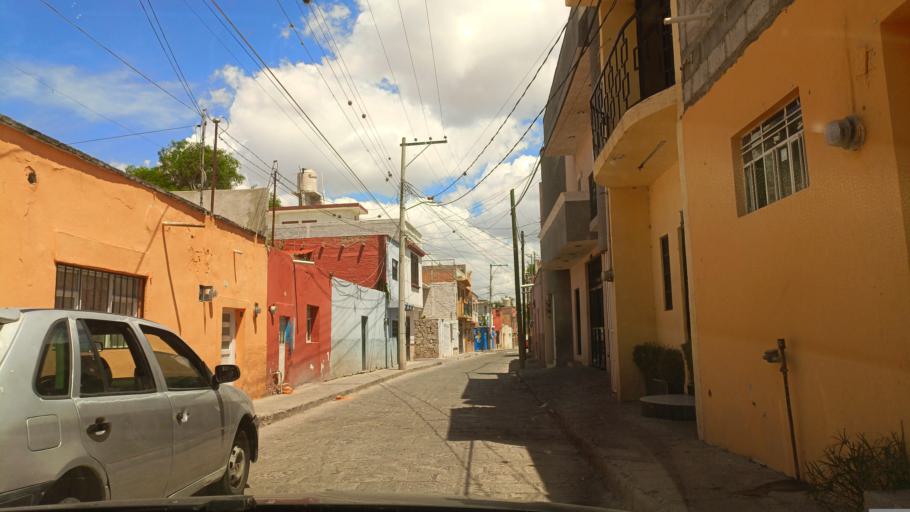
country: MX
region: Guanajuato
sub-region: San Luis de la Paz
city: San Luis de la Paz
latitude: 21.3037
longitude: -100.5160
